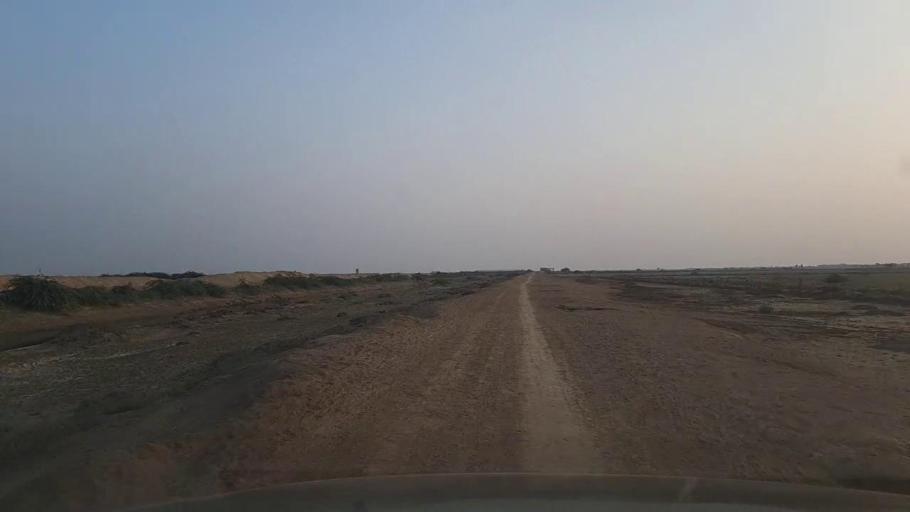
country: PK
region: Sindh
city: Jati
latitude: 24.5350
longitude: 68.4086
